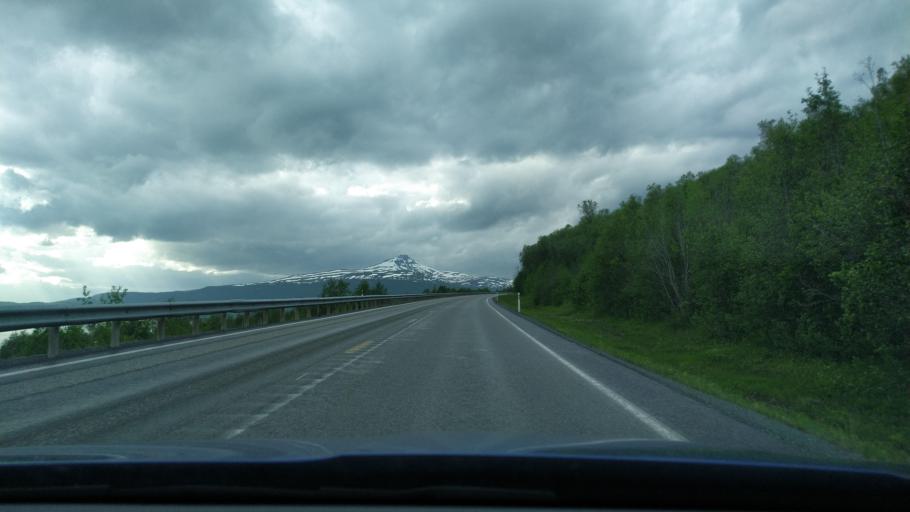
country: NO
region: Troms
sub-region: Balsfjord
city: Storsteinnes
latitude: 69.2430
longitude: 19.4542
